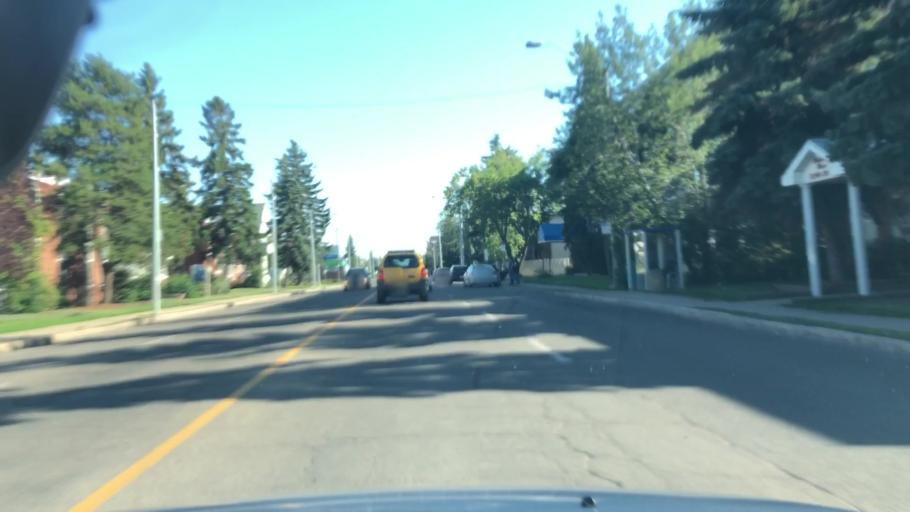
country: CA
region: Alberta
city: Edmonton
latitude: 53.5636
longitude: -113.5360
